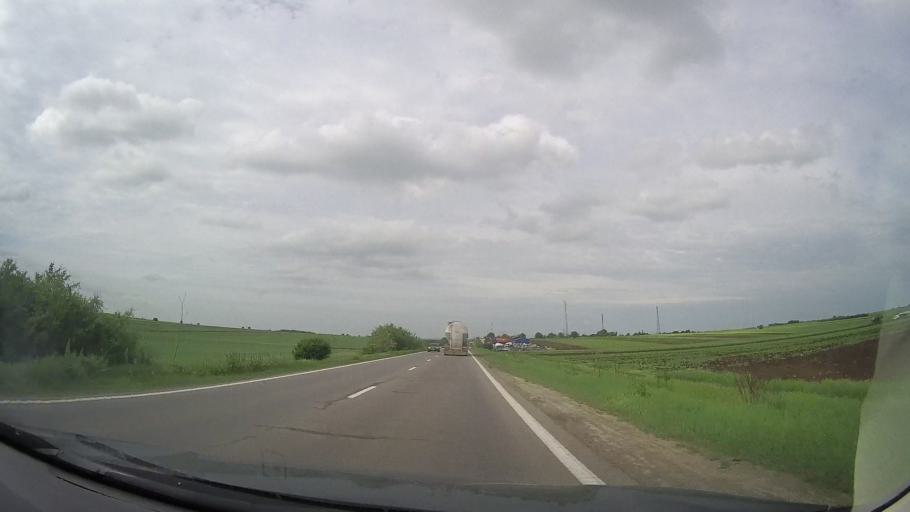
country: RO
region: Teleorman
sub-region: Comuna Vitanesti
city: Vitanesti
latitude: 44.0190
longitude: 25.4343
